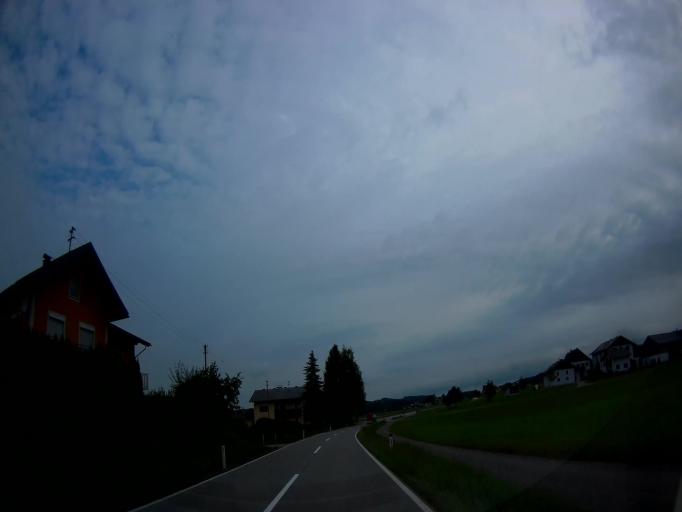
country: AT
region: Salzburg
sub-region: Politischer Bezirk Salzburg-Umgebung
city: Mattsee
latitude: 48.0007
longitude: 13.1221
